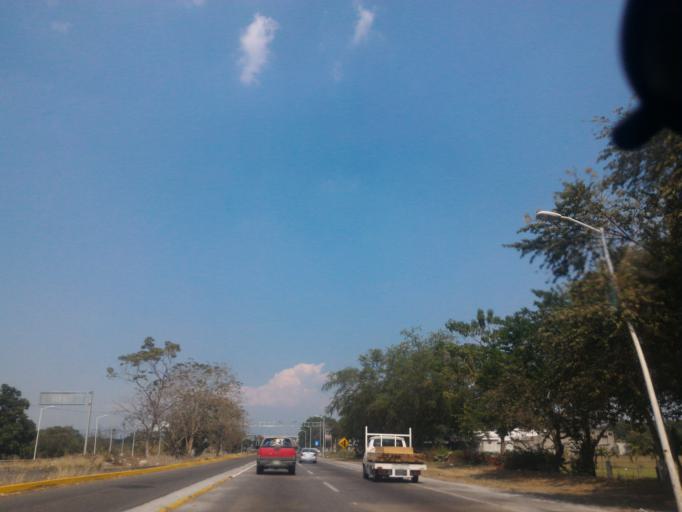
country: MX
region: Colima
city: Colima
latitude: 19.2069
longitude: -103.7423
